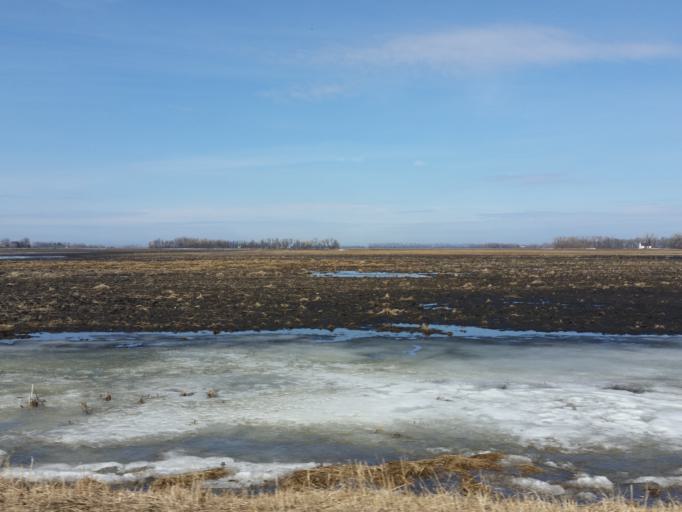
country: US
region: North Dakota
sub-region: Walsh County
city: Grafton
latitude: 48.4414
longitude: -97.4147
